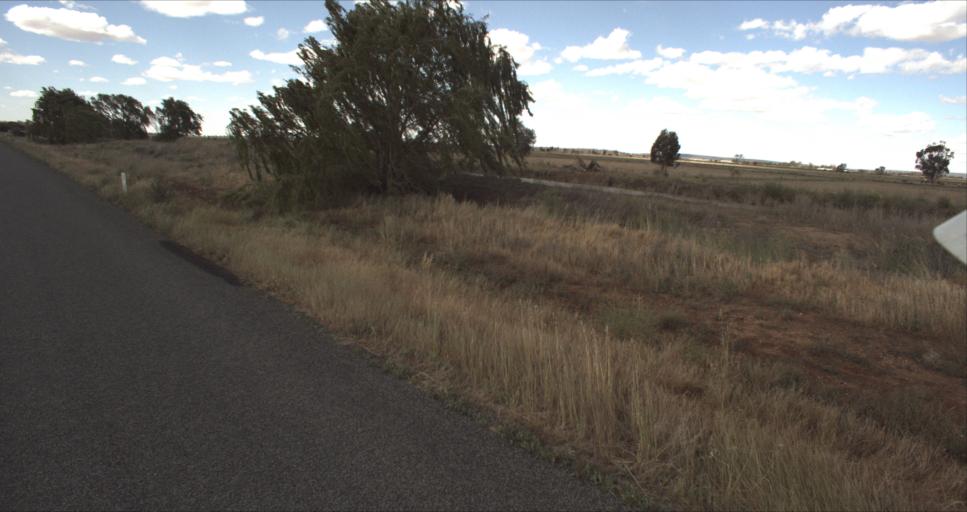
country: AU
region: New South Wales
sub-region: Leeton
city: Leeton
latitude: -34.4458
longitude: 146.2555
